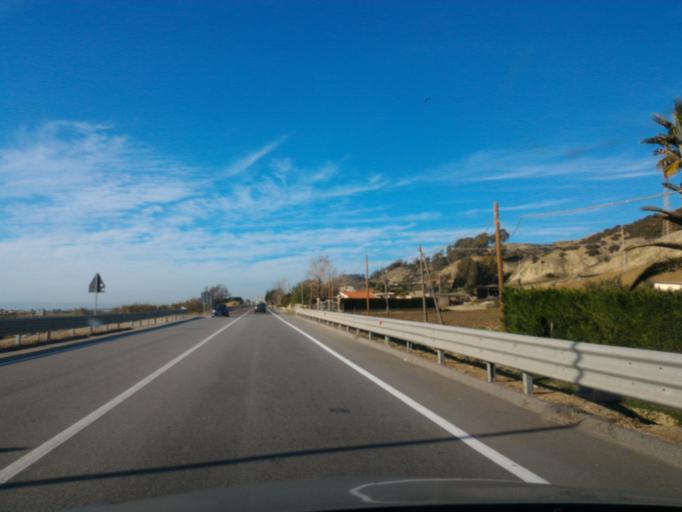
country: IT
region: Calabria
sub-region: Provincia di Crotone
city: Le Castella
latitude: 38.9469
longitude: 16.9435
